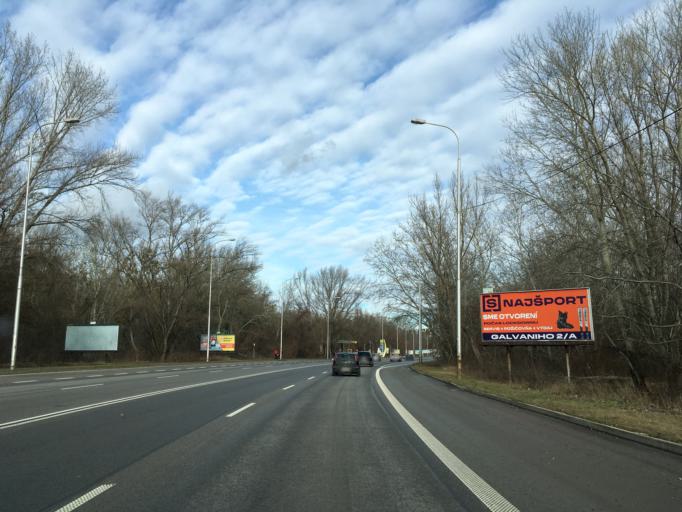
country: SK
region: Bratislavsky
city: Bratislava
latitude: 48.1044
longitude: 17.1218
